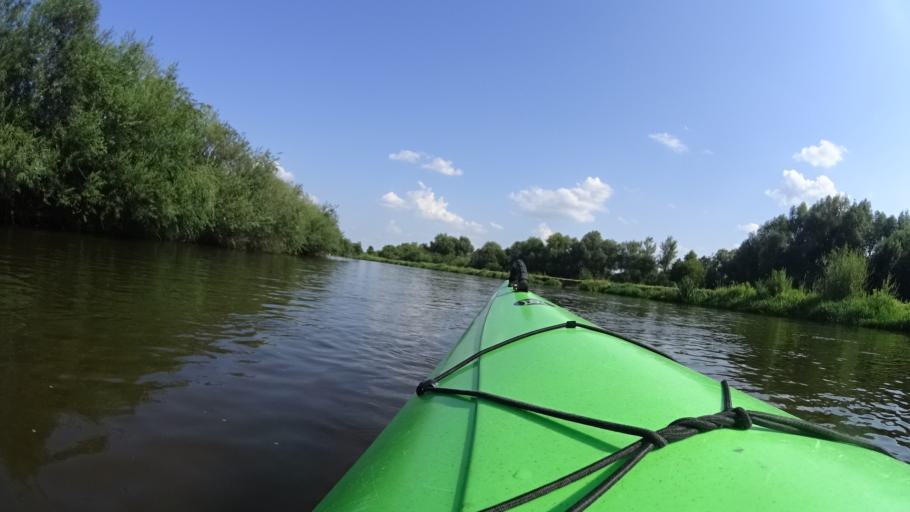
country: PL
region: Masovian Voivodeship
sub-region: Powiat bialobrzeski
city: Bialobrzegi
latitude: 51.6646
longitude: 20.8935
